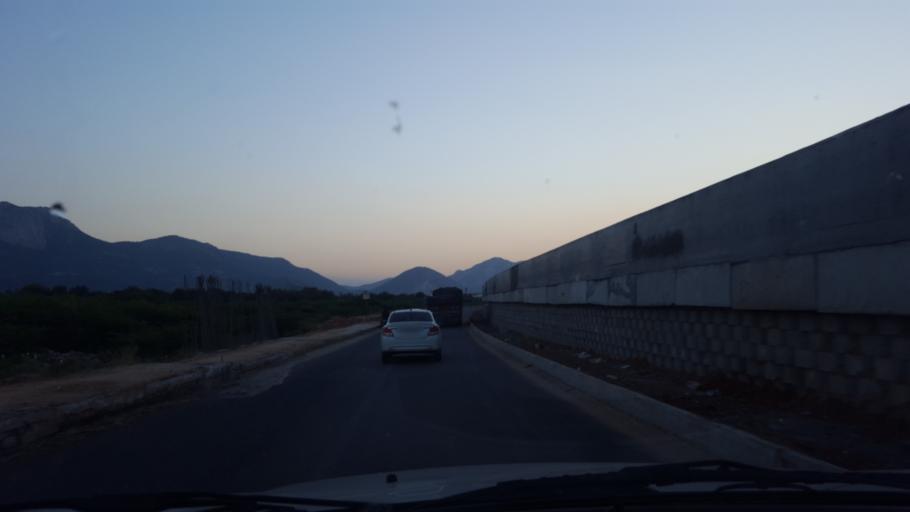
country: IN
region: Andhra Pradesh
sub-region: Chittoor
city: Narasingapuram
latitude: 13.5900
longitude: 79.3446
